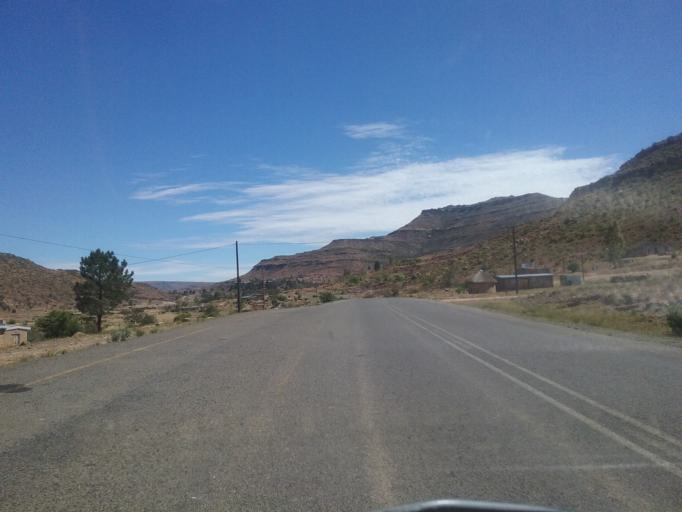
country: LS
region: Quthing
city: Quthing
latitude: -30.3547
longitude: 27.5454
